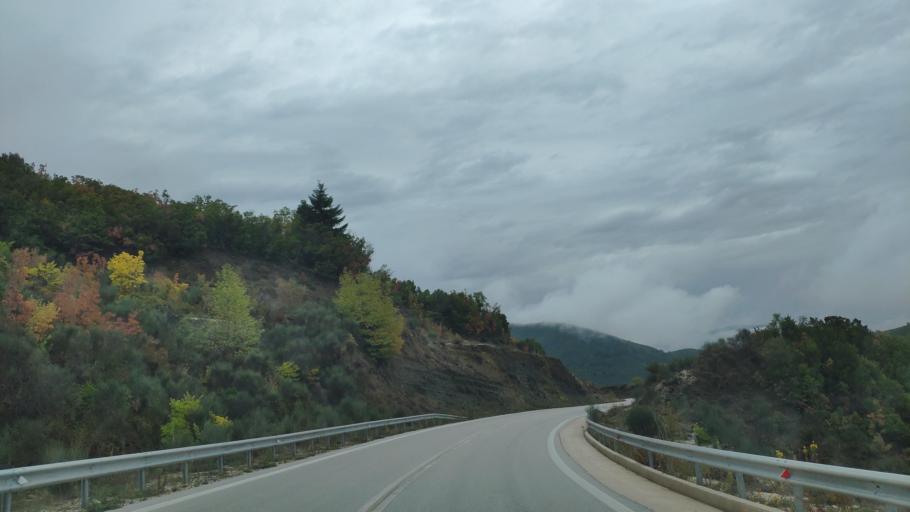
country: GR
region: Epirus
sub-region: Nomos Thesprotias
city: Paramythia
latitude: 39.4819
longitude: 20.6735
